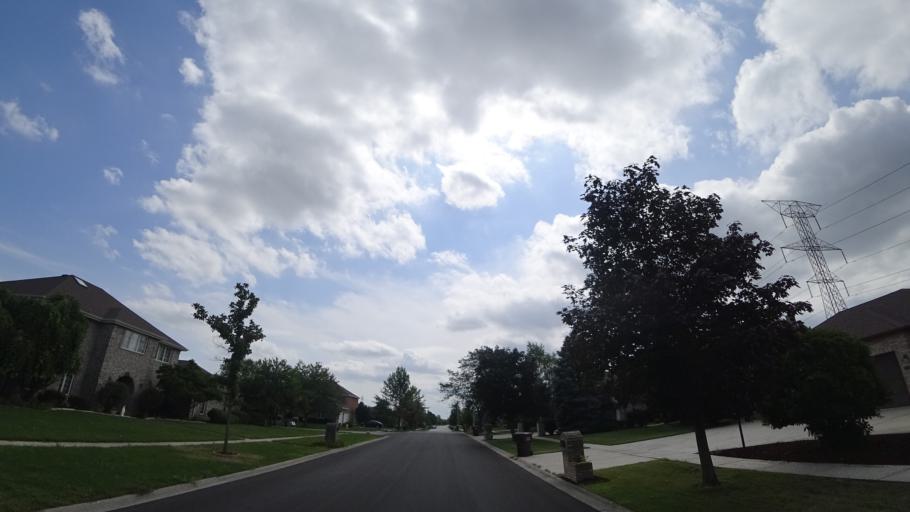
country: US
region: Illinois
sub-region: Cook County
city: Orland Hills
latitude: 41.5665
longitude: -87.8167
